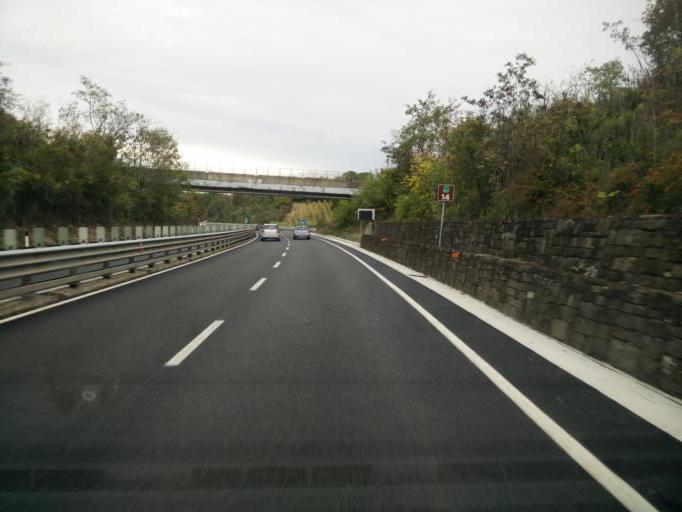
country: IT
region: Tuscany
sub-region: Province of Florence
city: Sambuca
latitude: 43.5374
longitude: 11.2206
